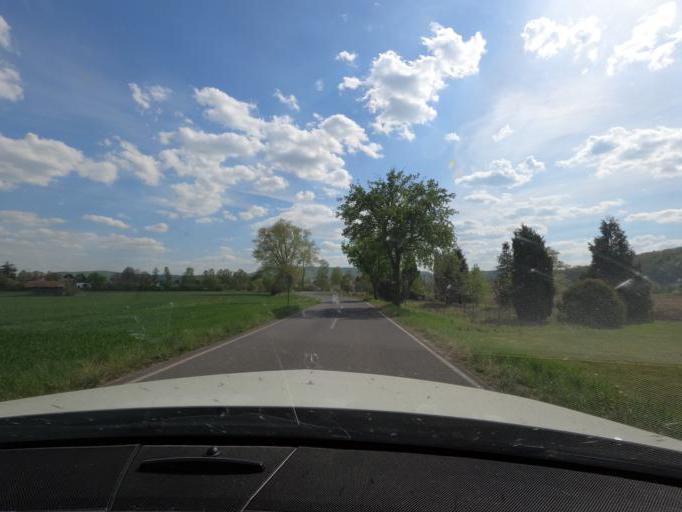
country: DE
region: Hesse
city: Wanfried
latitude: 51.1547
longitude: 10.1772
